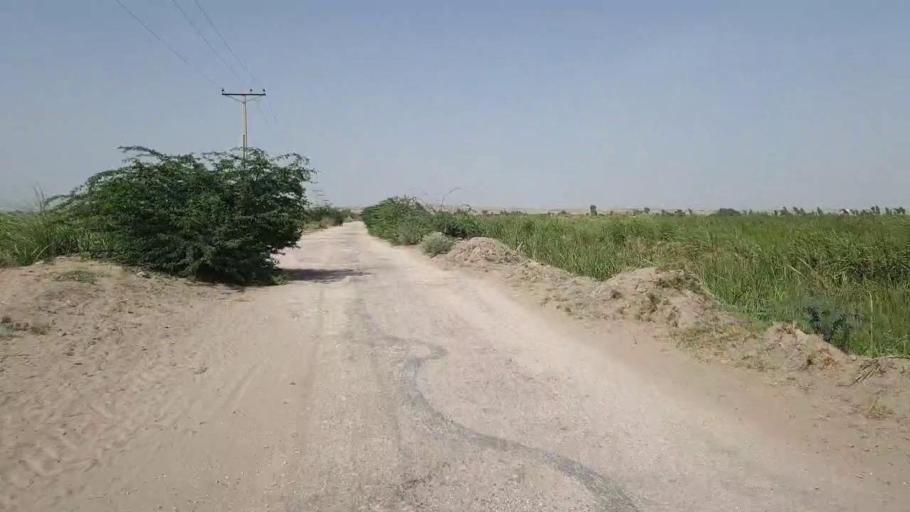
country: PK
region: Sindh
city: Jam Sahib
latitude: 26.4288
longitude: 68.9123
